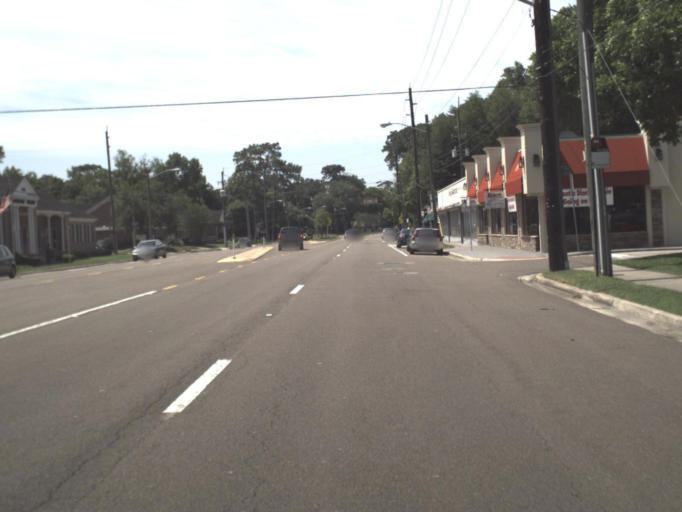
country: US
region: Florida
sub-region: Duval County
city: Jacksonville
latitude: 30.2922
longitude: -81.6485
